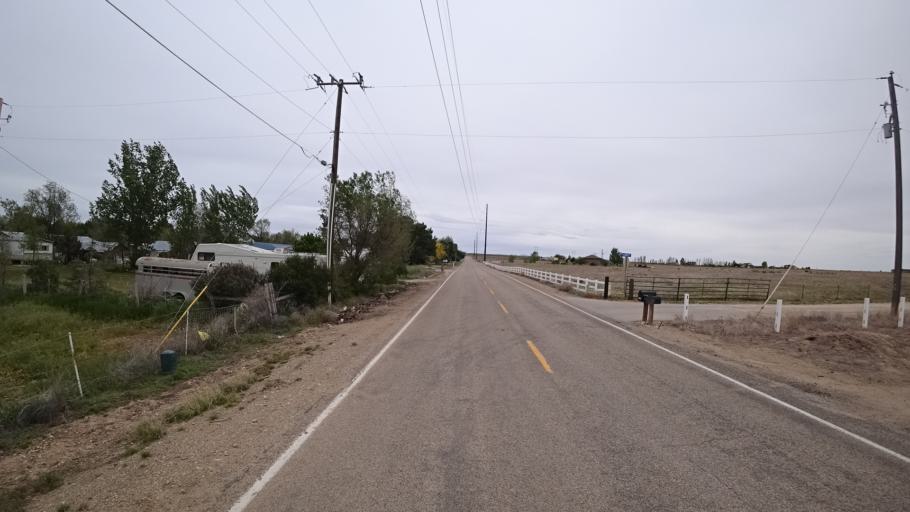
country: US
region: Idaho
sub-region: Ada County
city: Kuna
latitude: 43.4884
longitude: -116.3044
